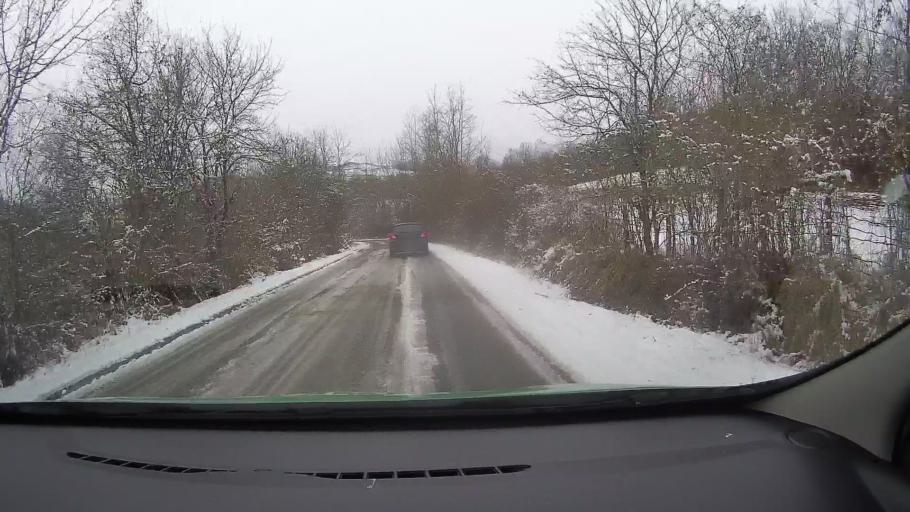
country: RO
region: Alba
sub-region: Comuna Almasu Mare
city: Almasu Mare
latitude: 46.0809
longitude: 23.1254
